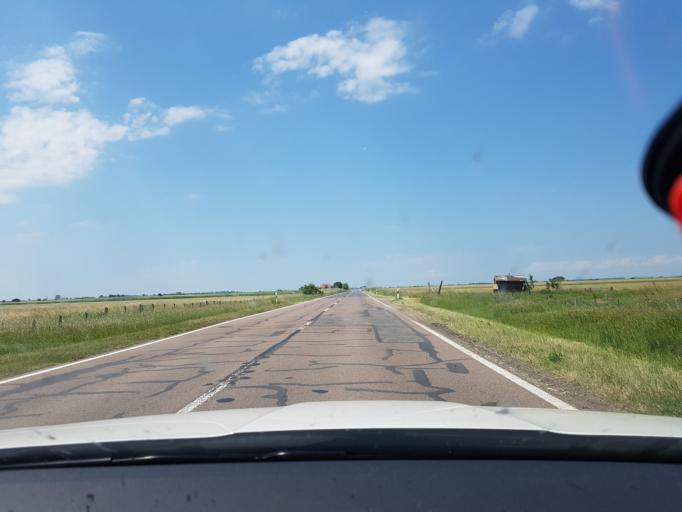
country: HU
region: Hajdu-Bihar
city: Hortobagy
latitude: 47.5895
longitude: 21.0899
